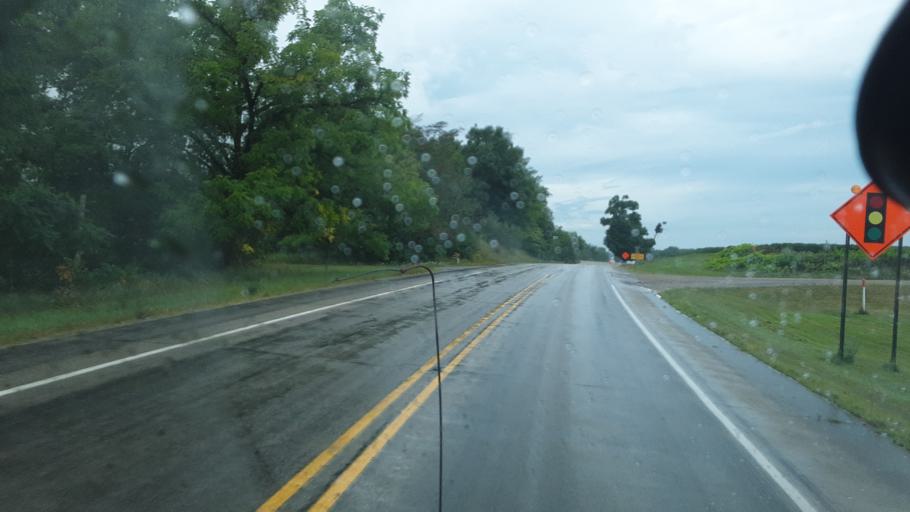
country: US
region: Indiana
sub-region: Steuben County
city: Hamilton
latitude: 41.6308
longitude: -84.8121
